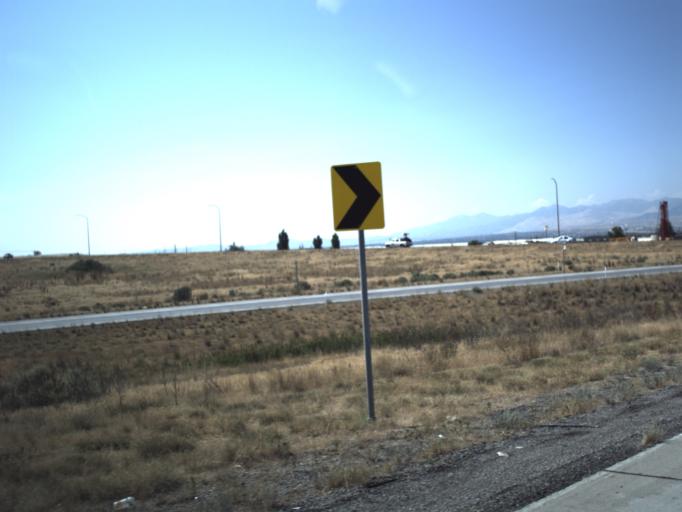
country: US
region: Utah
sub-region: Salt Lake County
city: Salt Lake City
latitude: 40.7634
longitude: -111.9524
